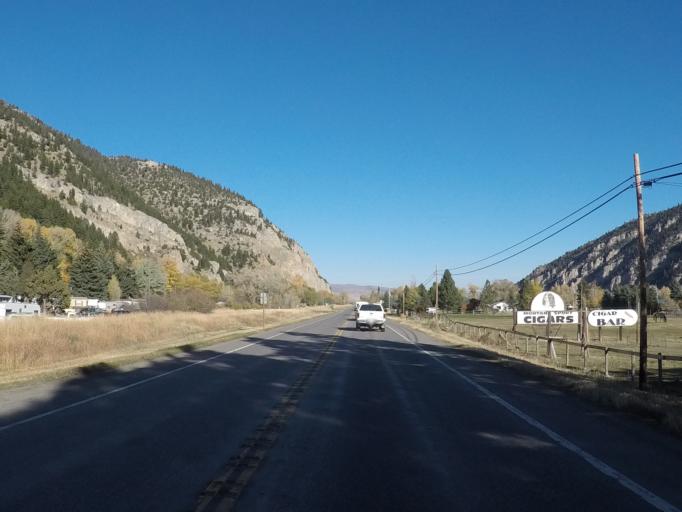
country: US
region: Montana
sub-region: Park County
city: Livingston
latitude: 45.6010
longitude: -110.5733
